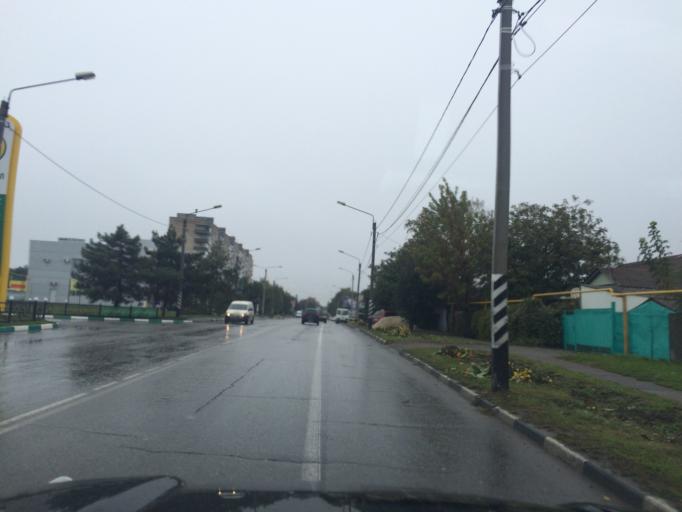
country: RU
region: Rostov
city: Azov
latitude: 47.0906
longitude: 39.4537
